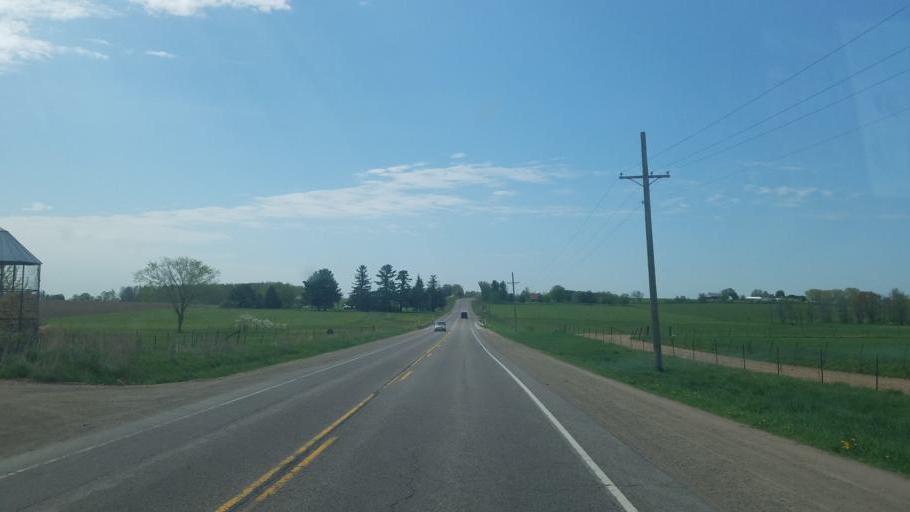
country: US
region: Wisconsin
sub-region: Marathon County
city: Spencer
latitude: 44.5932
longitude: -90.3764
